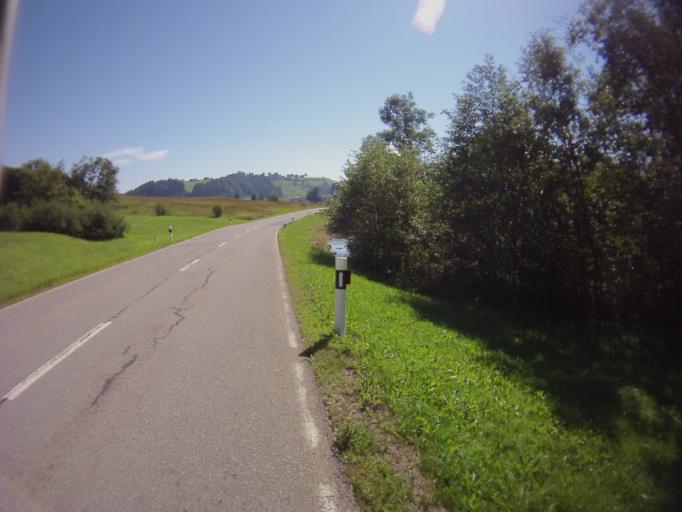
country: CH
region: Schwyz
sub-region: Bezirk Hoefe
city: Schindellegi
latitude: 47.1530
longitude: 8.7123
